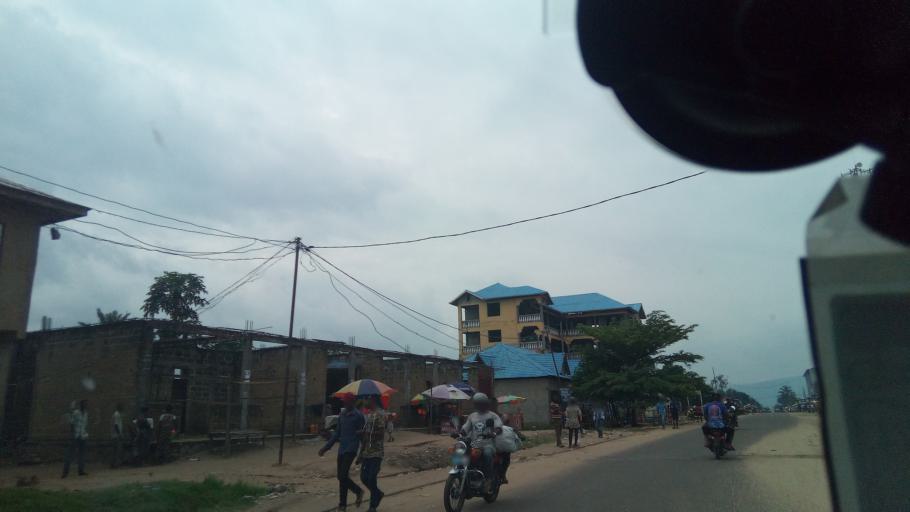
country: CG
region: Brazzaville
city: Brazzaville
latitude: -4.0559
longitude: 15.5549
